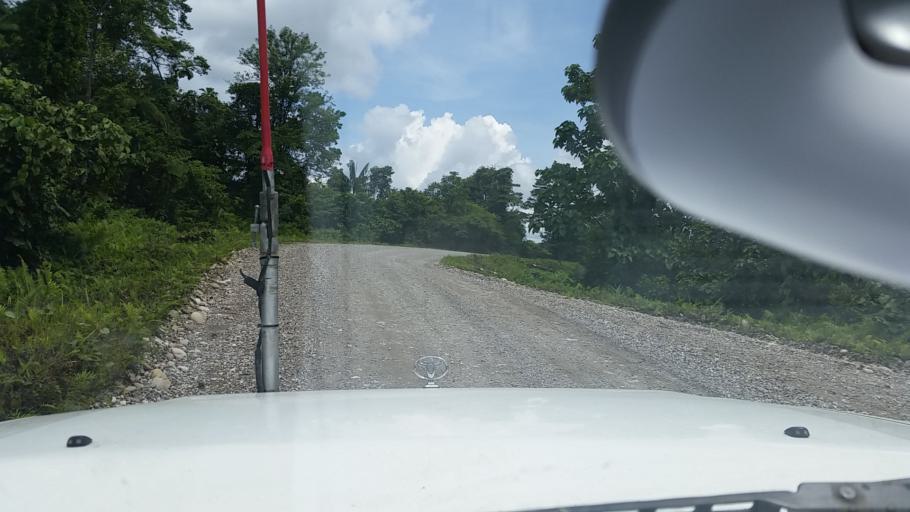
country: PG
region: Western Province
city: Kiunga
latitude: -5.6403
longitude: 141.1835
